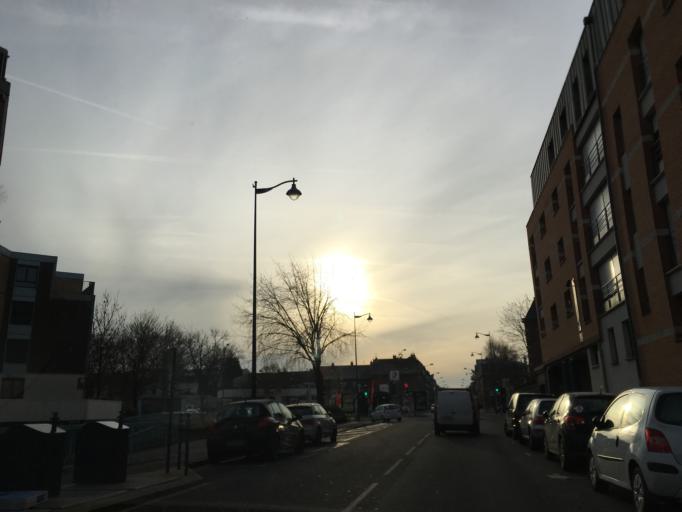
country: FR
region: Nord-Pas-de-Calais
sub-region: Departement du Pas-de-Calais
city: Arras
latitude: 50.2915
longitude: 2.7834
